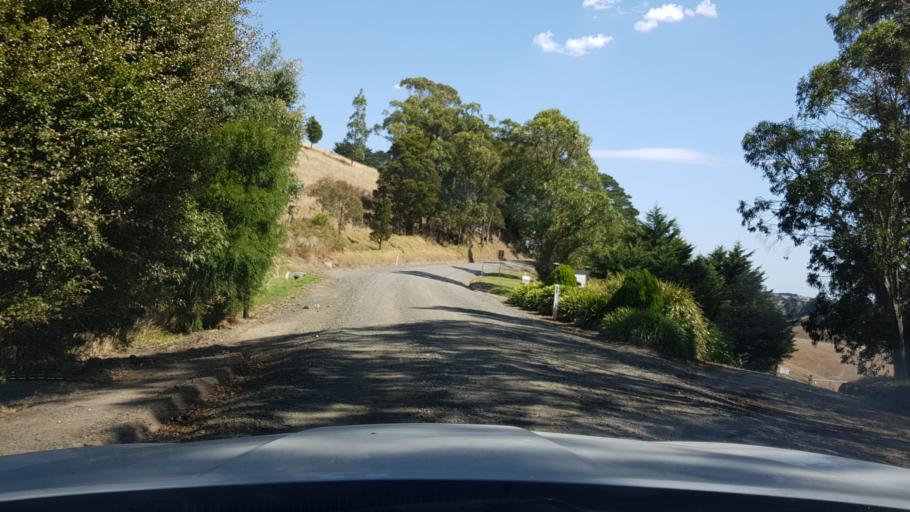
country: AU
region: Victoria
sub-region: Baw Baw
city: Warragul
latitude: -38.2900
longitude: 145.9168
